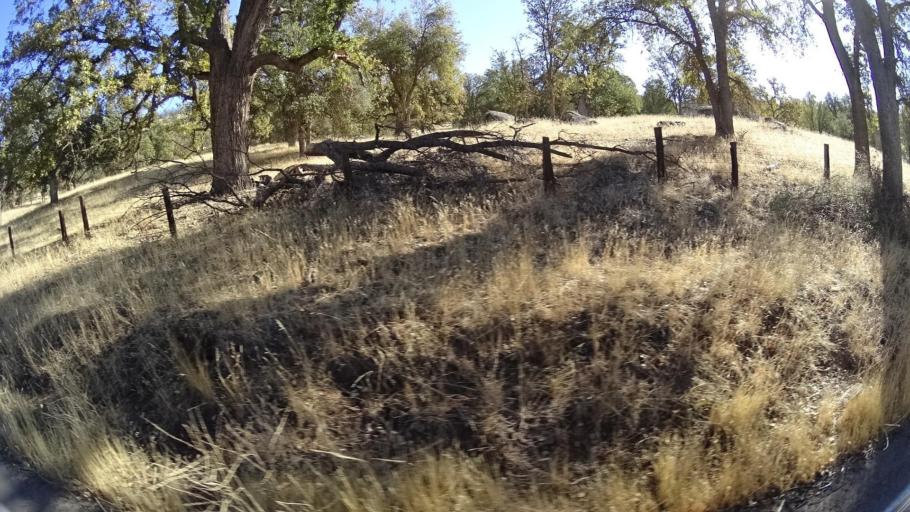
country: US
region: California
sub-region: Kern County
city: Alta Sierra
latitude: 35.7472
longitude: -118.7174
